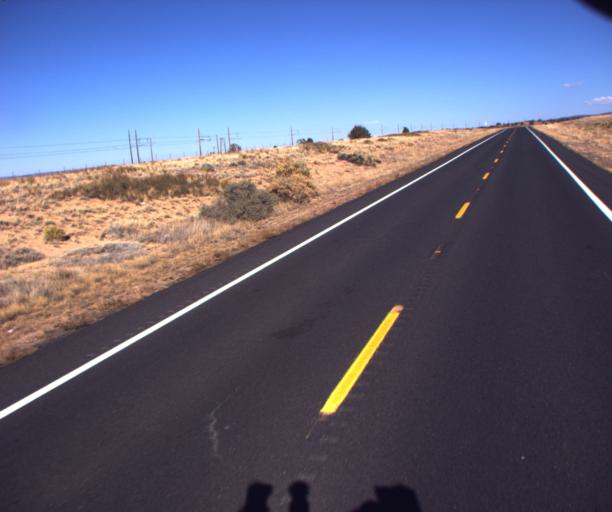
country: US
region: Arizona
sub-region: Coconino County
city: Kaibito
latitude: 36.4379
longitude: -110.7564
